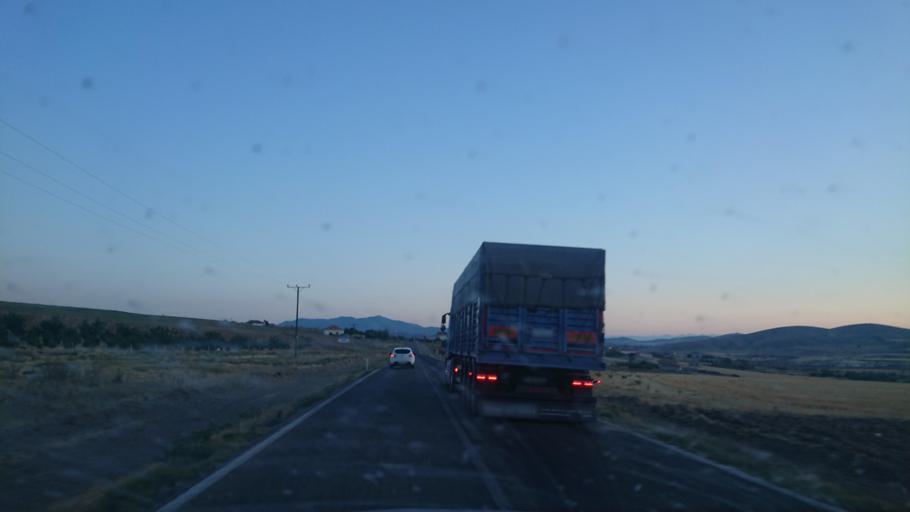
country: TR
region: Aksaray
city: Balci
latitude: 38.7998
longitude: 34.1289
